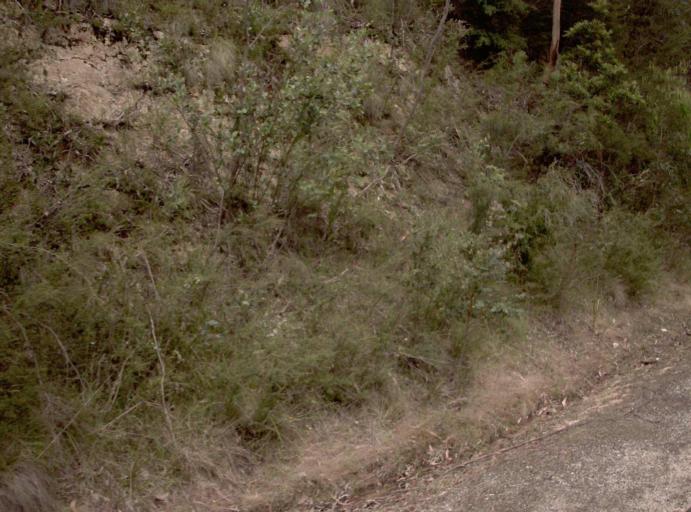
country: AU
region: New South Wales
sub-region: Bombala
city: Bombala
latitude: -37.3426
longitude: 149.2053
